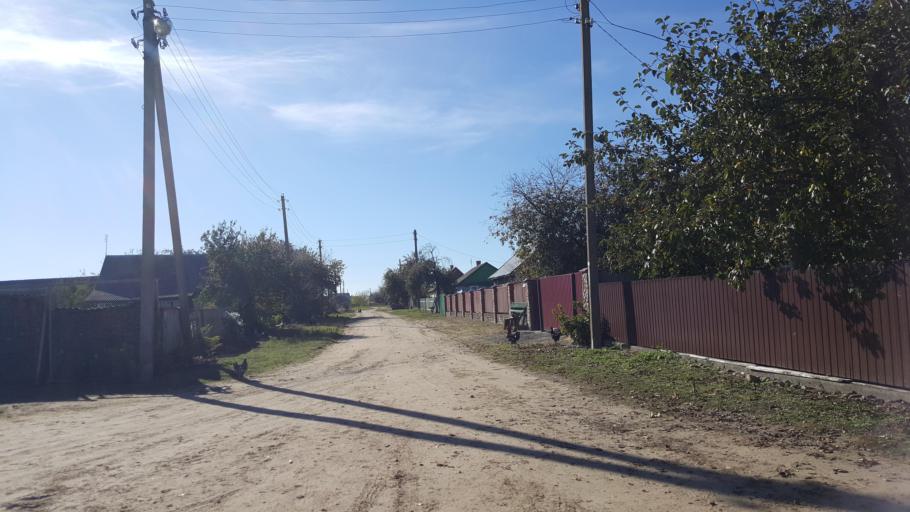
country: BY
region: Brest
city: Kamyanyets
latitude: 52.4071
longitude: 23.8005
